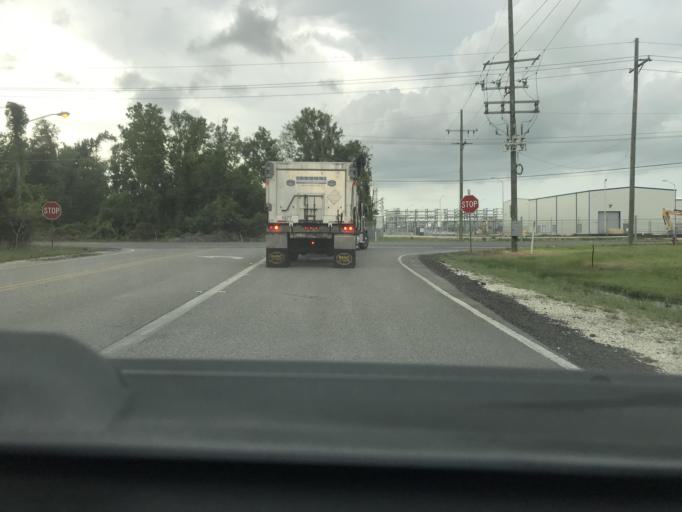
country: US
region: Louisiana
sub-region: Calcasieu Parish
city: Westlake
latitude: 30.2460
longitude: -93.2911
